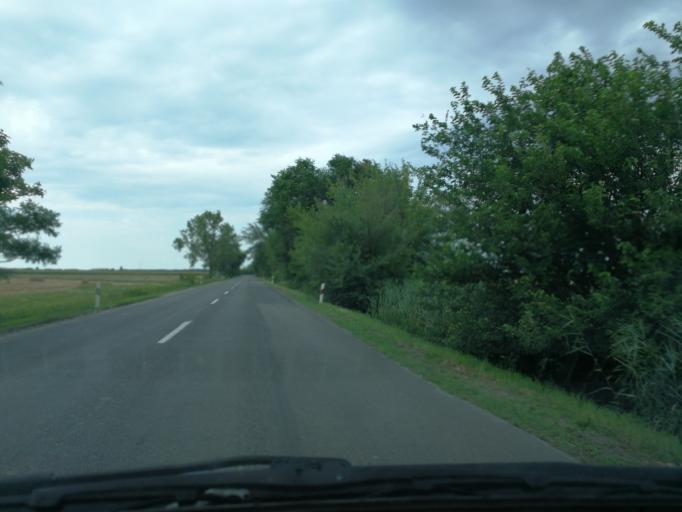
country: HU
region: Bacs-Kiskun
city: Dusnok
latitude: 46.4107
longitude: 18.9458
